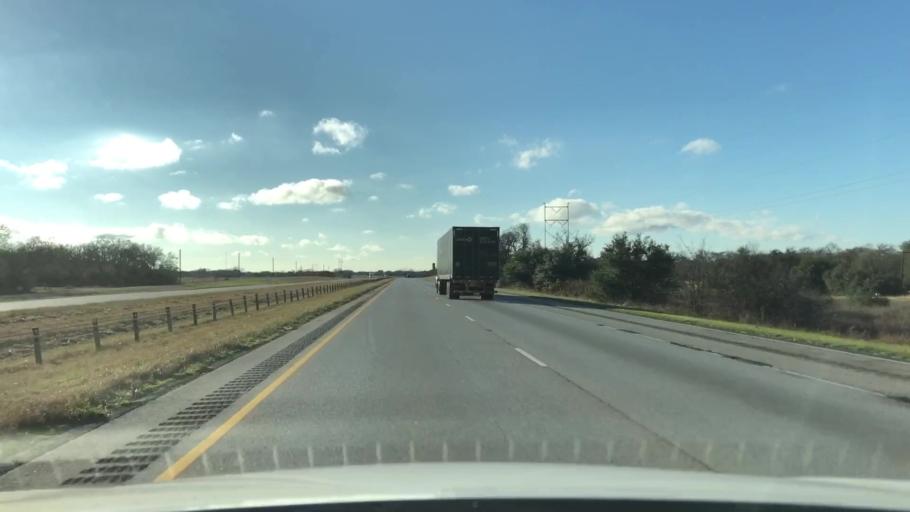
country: US
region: Texas
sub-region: Colorado County
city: Weimar
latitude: 29.6893
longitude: -96.6878
